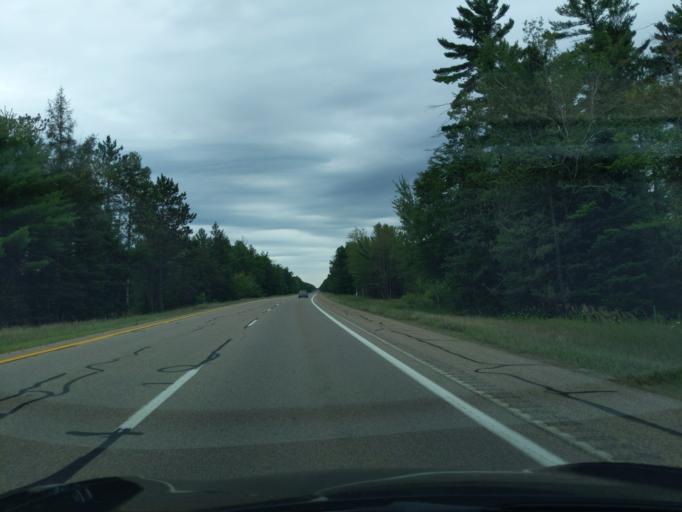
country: US
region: Michigan
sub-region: Roscommon County
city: Houghton Lake
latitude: 44.2230
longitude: -84.7970
